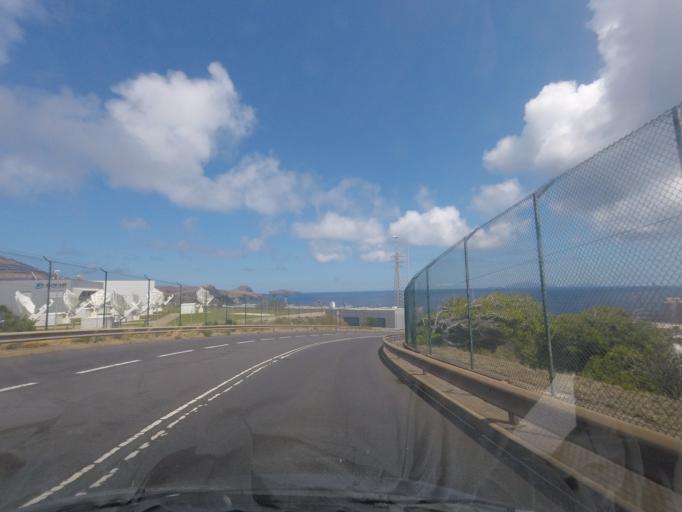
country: PT
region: Madeira
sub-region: Machico
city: Canical
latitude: 32.7420
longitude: -16.7352
